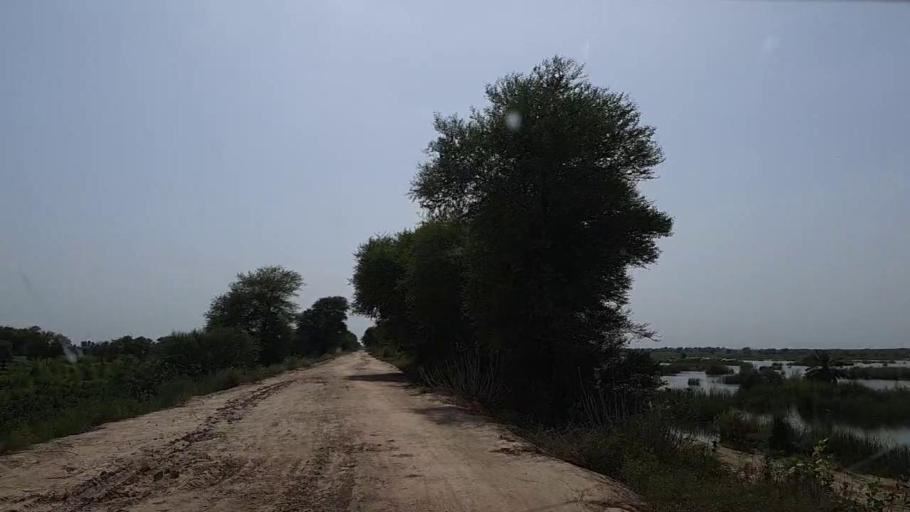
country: PK
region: Sindh
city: Ghotki
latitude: 28.0866
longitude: 69.4090
